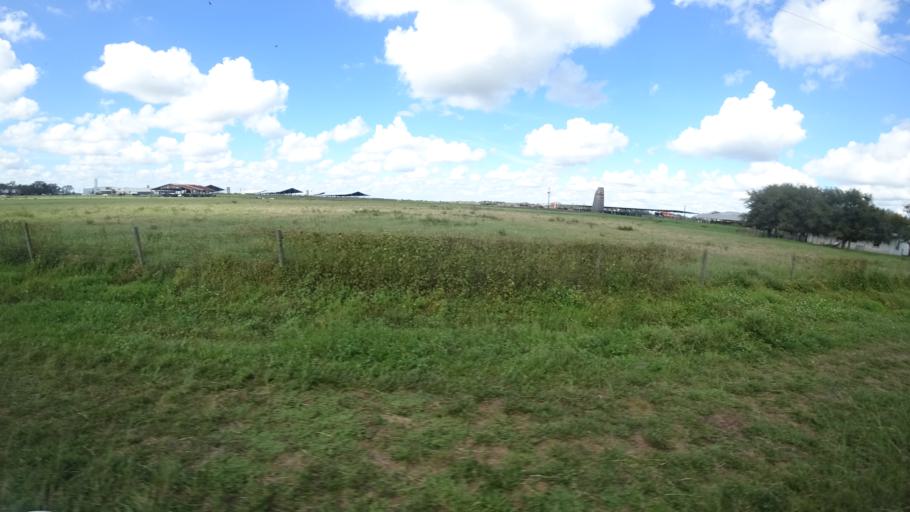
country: US
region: Florida
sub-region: Sarasota County
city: Lake Sarasota
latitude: 27.3632
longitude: -82.2246
